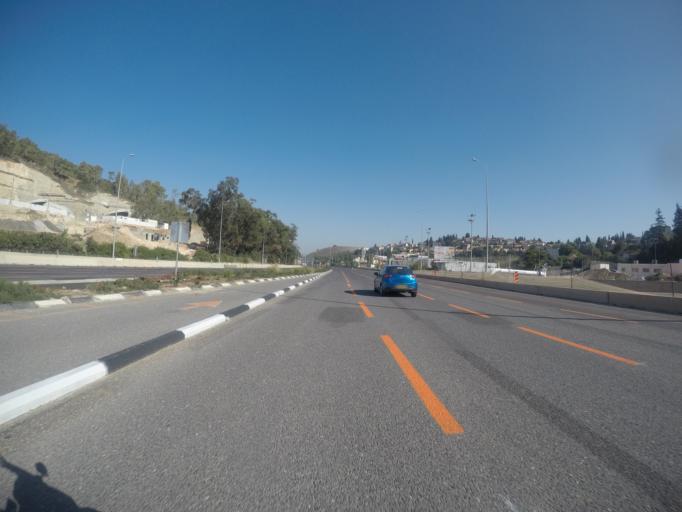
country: IL
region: Haifa
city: Daliyat el Karmil
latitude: 32.6581
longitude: 35.1023
